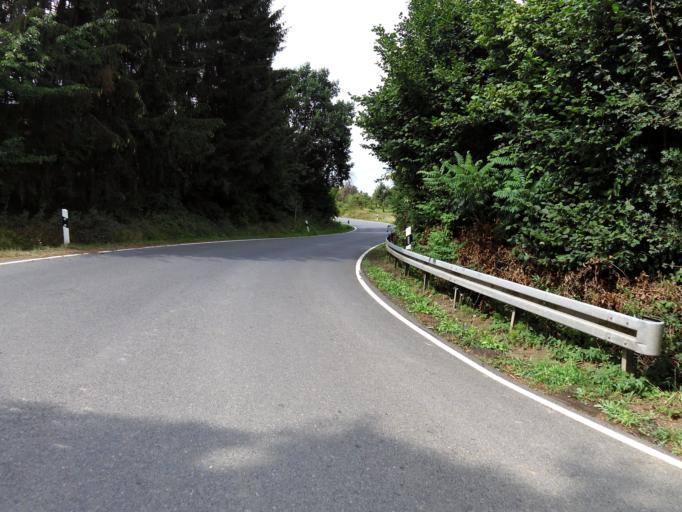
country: DE
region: Hesse
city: Hochst im Odenwald
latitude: 49.7743
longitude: 8.9600
